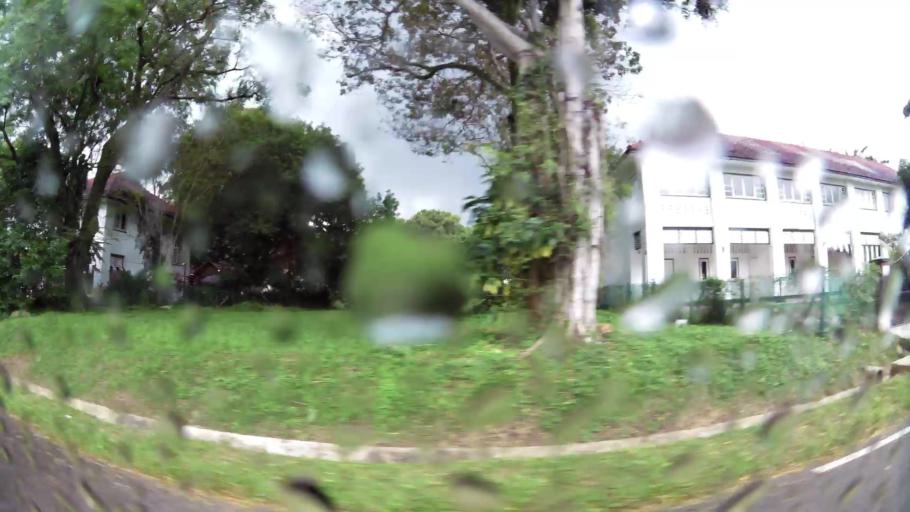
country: MY
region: Johor
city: Kampung Pasir Gudang Baru
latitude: 1.4082
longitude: 103.8704
